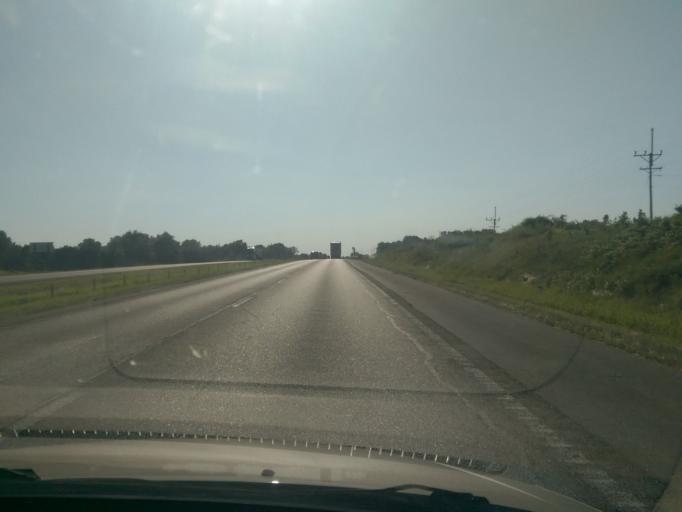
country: US
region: Missouri
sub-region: Lafayette County
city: Higginsville
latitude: 39.0022
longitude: -93.7958
